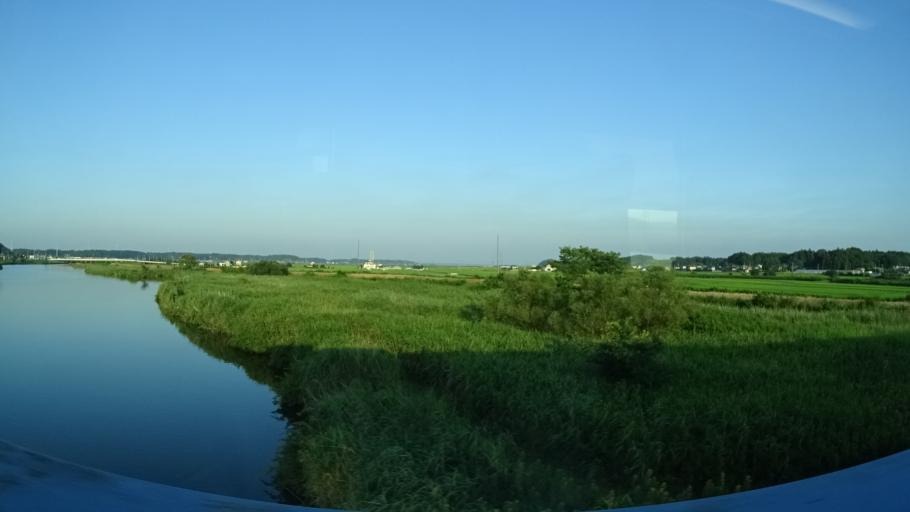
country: JP
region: Ibaraki
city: Ishioka
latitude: 36.1596
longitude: 140.2920
